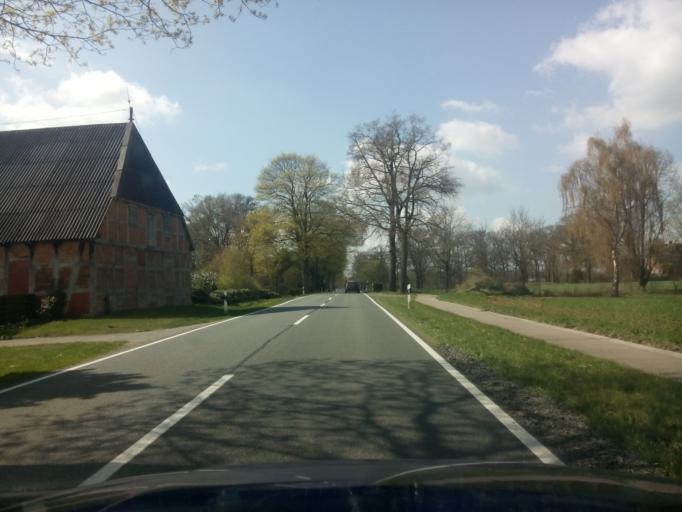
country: DE
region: Lower Saxony
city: Lilienthal
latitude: 53.1769
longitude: 8.8866
